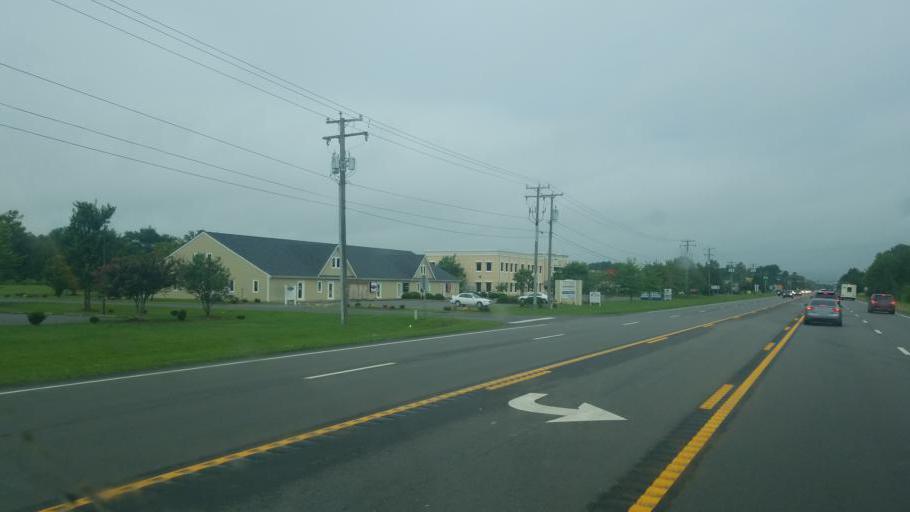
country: US
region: North Carolina
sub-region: Currituck County
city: Moyock
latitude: 36.5149
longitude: -76.1669
